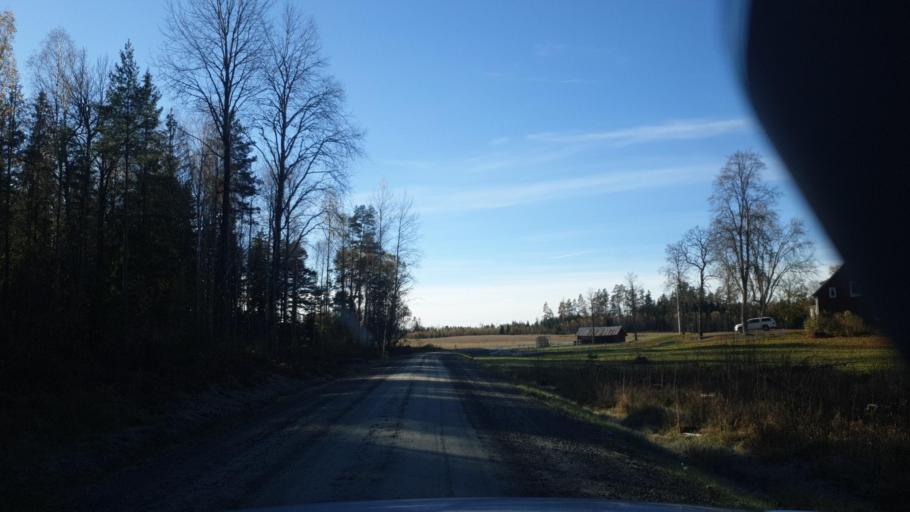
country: SE
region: Vaermland
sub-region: Karlstads Kommun
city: Edsvalla
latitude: 59.4488
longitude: 13.1225
